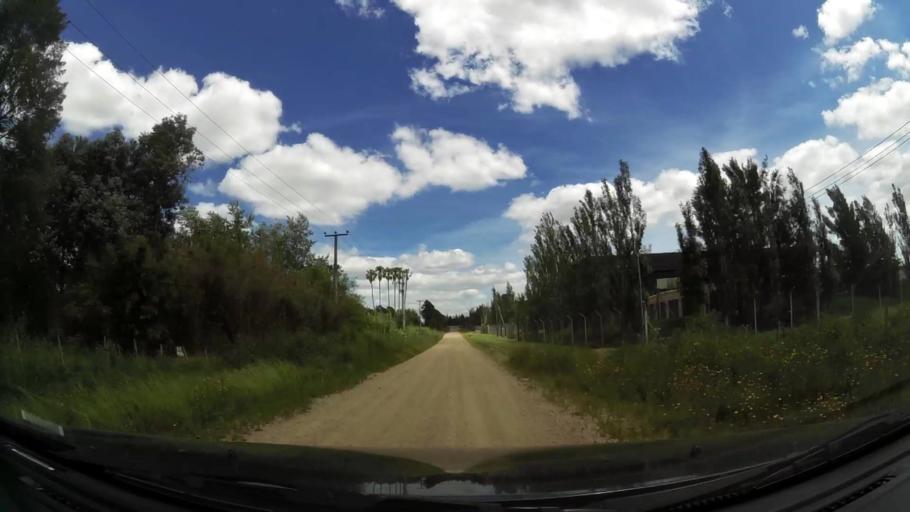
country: UY
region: Canelones
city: Colonia Nicolich
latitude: -34.8032
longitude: -56.0001
